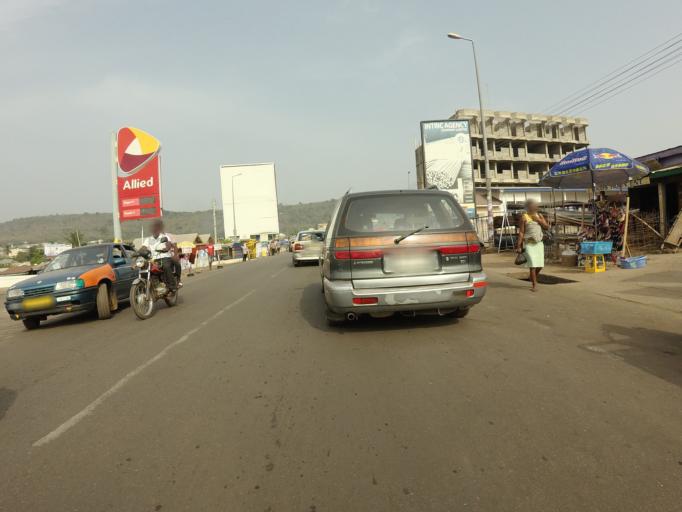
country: GH
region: Volta
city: Ho
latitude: 6.6170
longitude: 0.4727
